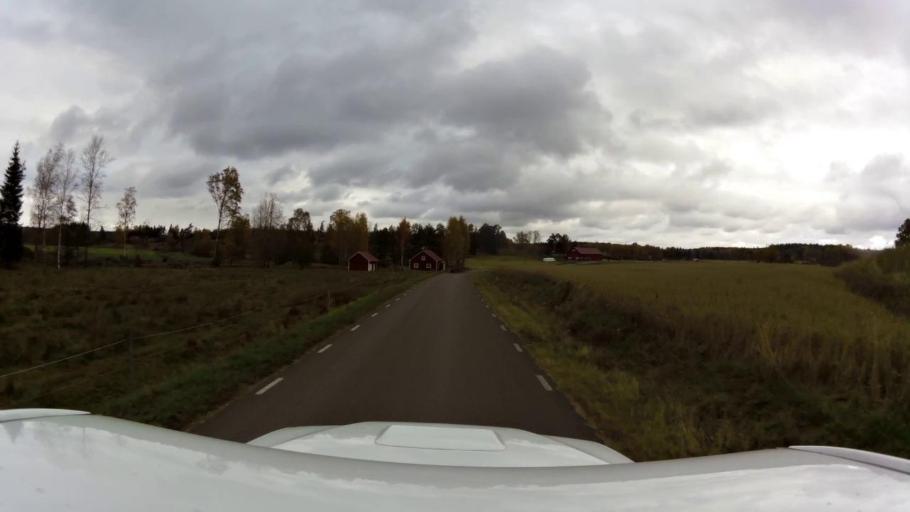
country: SE
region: OEstergoetland
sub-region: Motala Kommun
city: Borensberg
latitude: 58.5663
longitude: 15.3885
